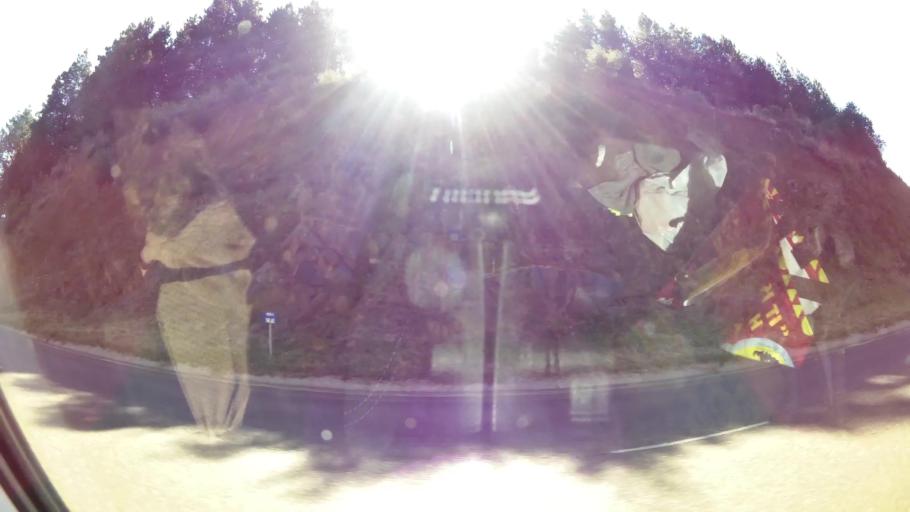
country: ZA
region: Limpopo
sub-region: Capricorn District Municipality
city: Mankoeng
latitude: -23.9397
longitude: 29.9497
